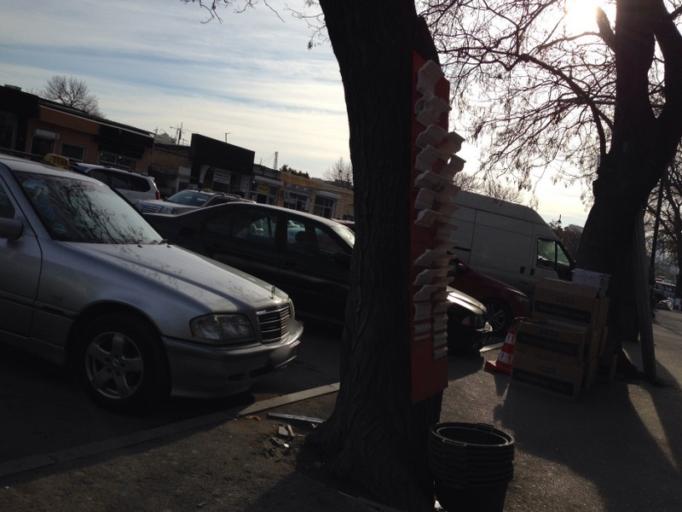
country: AZ
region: Baki
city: Baku
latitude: 40.3882
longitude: 49.8579
